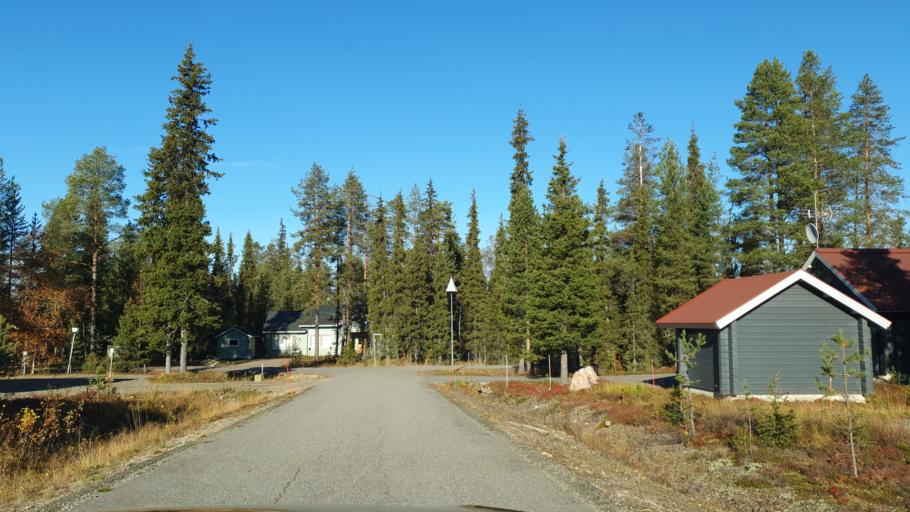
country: FI
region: Lapland
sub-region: Tunturi-Lappi
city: Kolari
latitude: 67.5991
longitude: 24.1797
